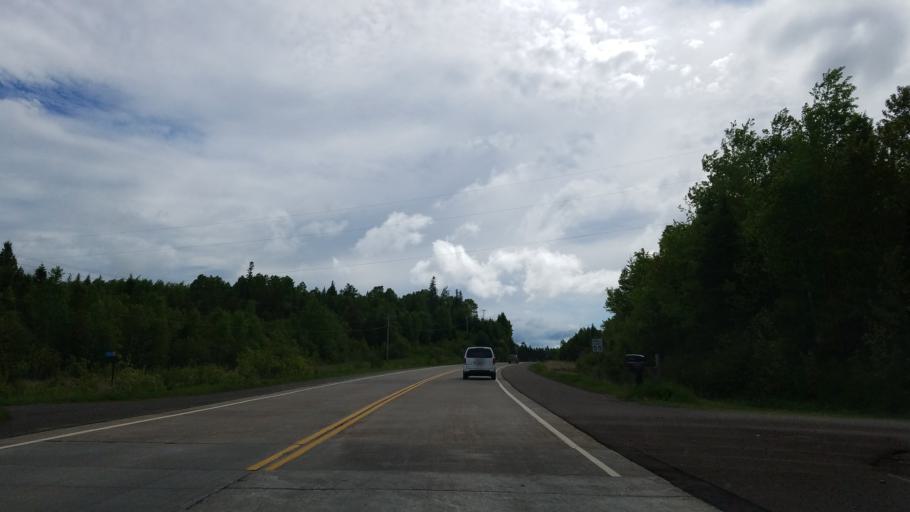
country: US
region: Minnesota
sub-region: Lake County
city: Two Harbors
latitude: 47.1015
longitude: -91.5447
